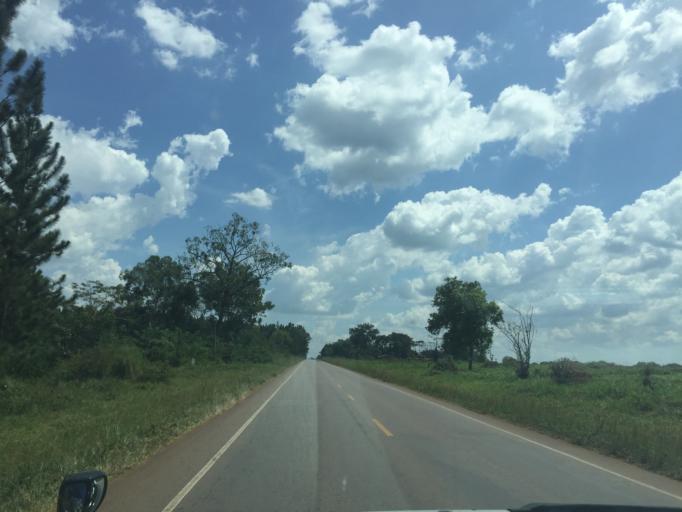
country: UG
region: Central Region
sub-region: Nakasongola District
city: Nakasongola
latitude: 1.1668
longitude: 32.4634
